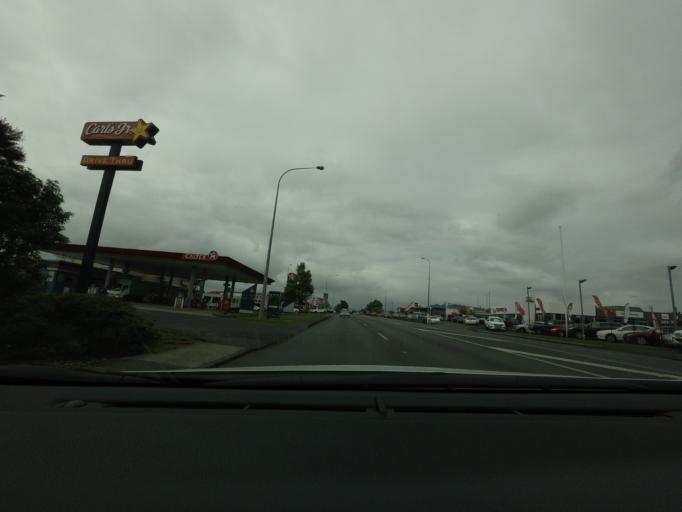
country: NZ
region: Auckland
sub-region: Auckland
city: Rosebank
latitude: -36.8543
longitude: 174.6301
